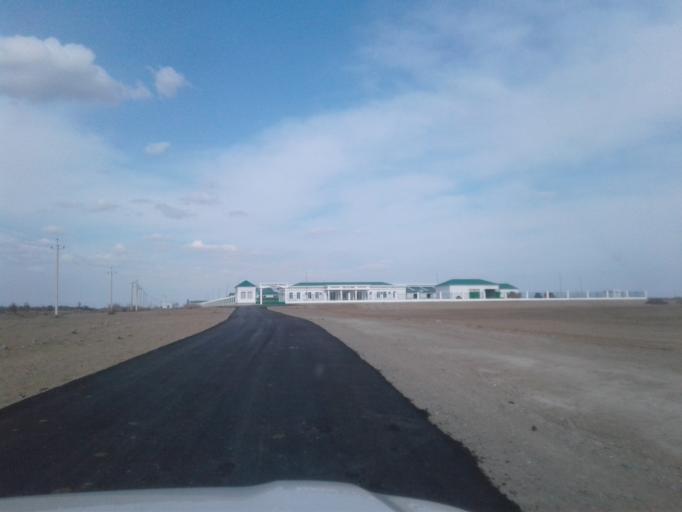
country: TM
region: Ahal
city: Ashgabat
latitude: 38.1942
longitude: 58.4192
